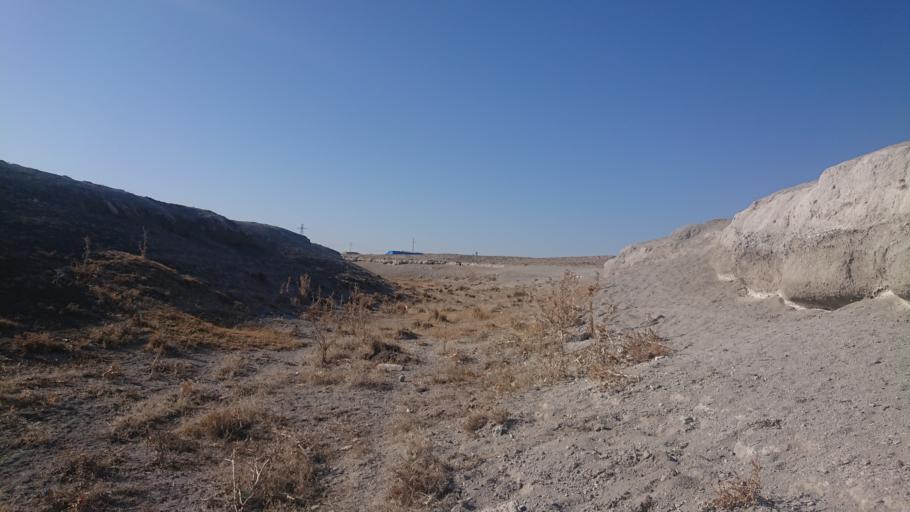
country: TR
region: Aksaray
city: Sultanhani
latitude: 38.2591
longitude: 33.5098
